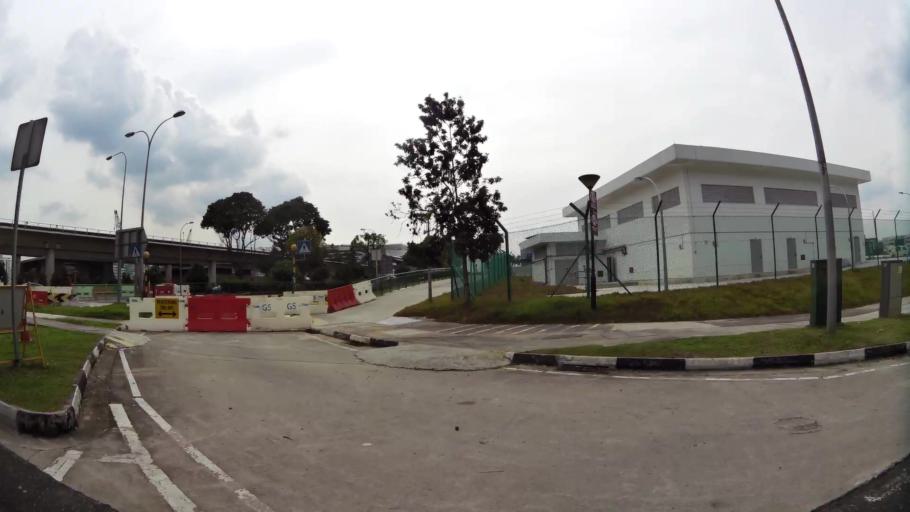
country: MY
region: Johor
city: Johor Bahru
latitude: 1.4385
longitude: 103.7887
